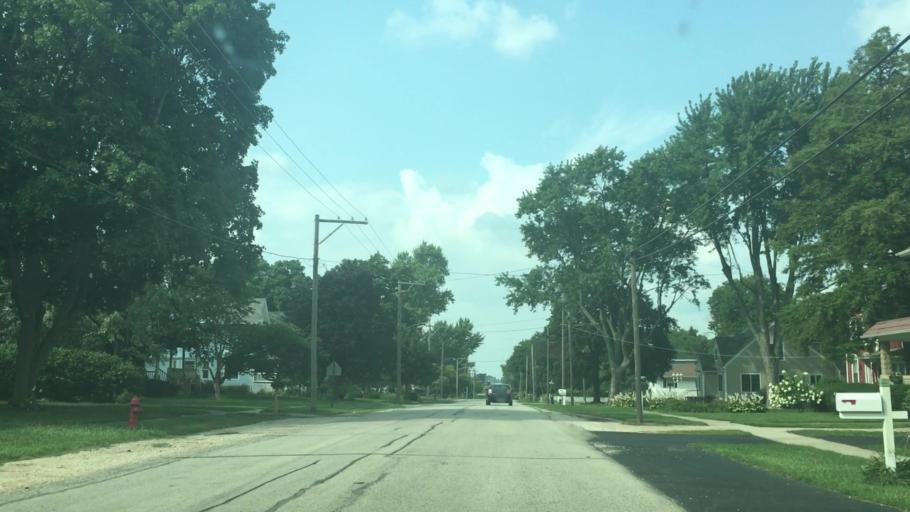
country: US
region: Illinois
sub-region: DeKalb County
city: Waterman
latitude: 41.7724
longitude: -88.7739
